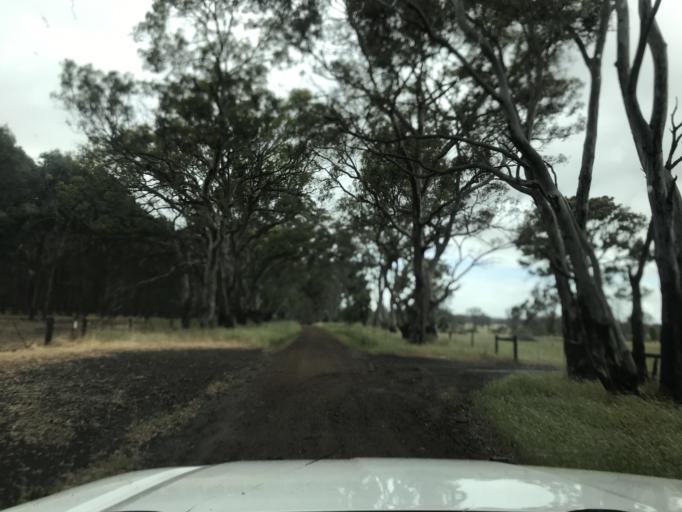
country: AU
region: South Australia
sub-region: Wattle Range
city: Penola
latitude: -37.2346
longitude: 141.4425
